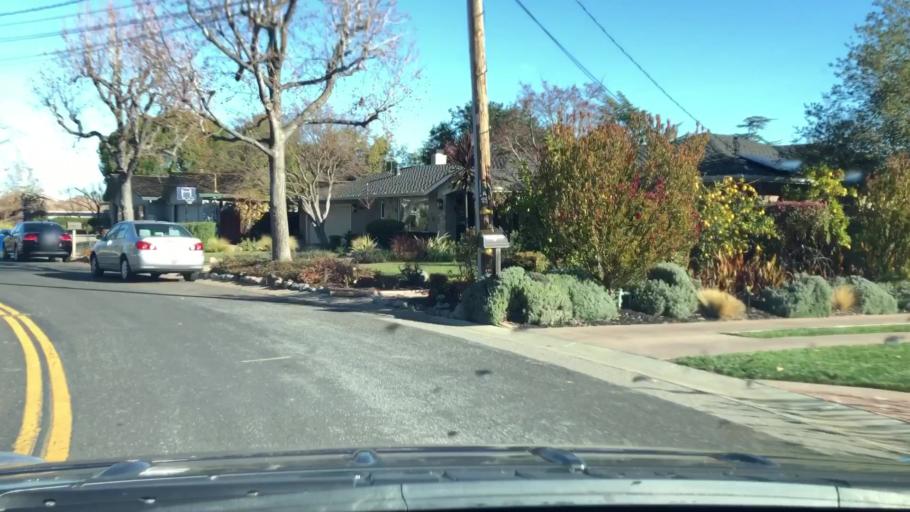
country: US
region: California
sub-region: Santa Clara County
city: Monte Sereno
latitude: 37.2544
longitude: -121.9727
